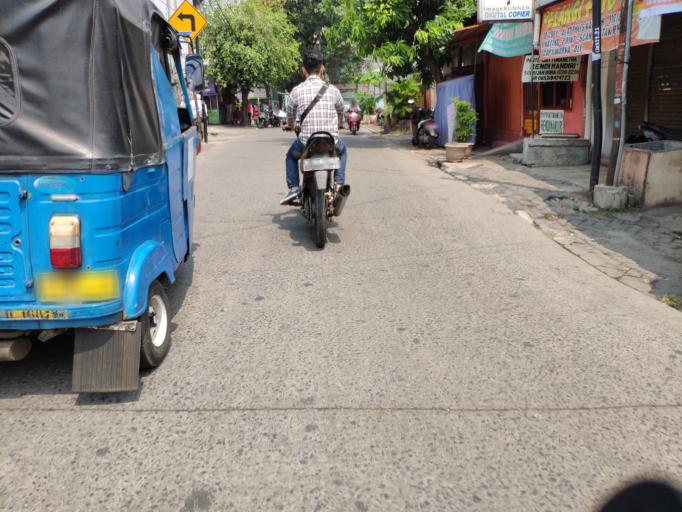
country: ID
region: Jakarta Raya
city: Jakarta
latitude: -6.2057
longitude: 106.8669
